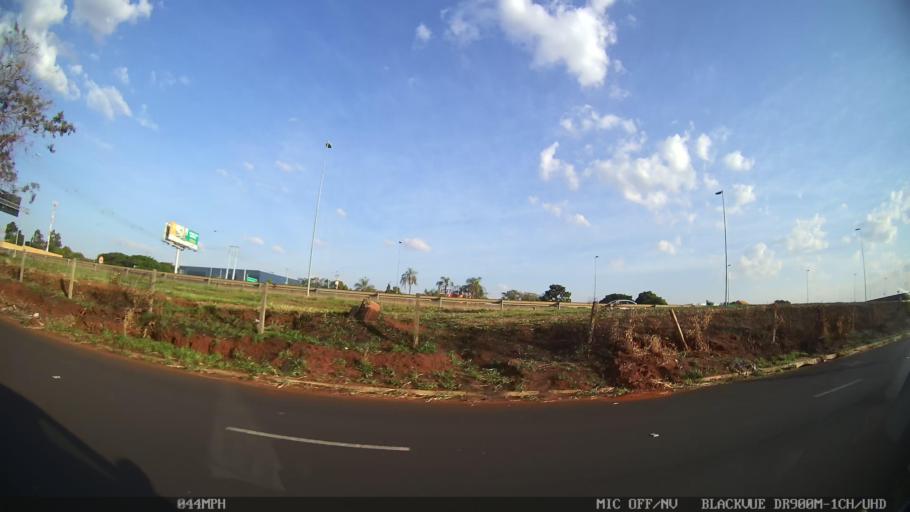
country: BR
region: Sao Paulo
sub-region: Ribeirao Preto
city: Ribeirao Preto
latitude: -21.2059
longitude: -47.7539
